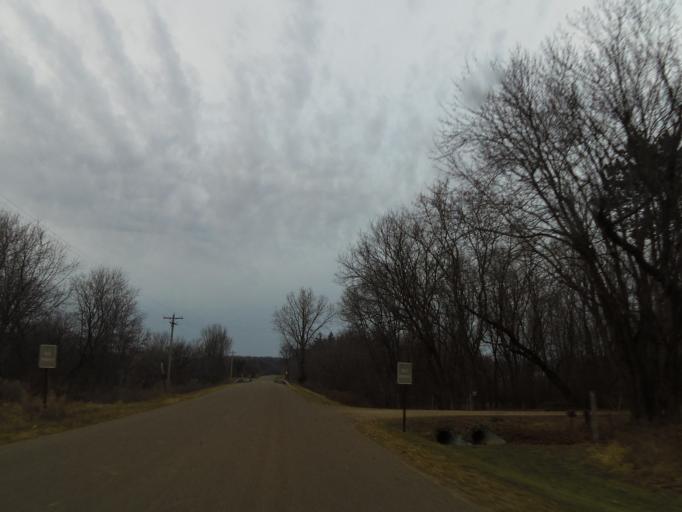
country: US
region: Wisconsin
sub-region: Pierce County
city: River Falls
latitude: 44.8897
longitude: -92.5984
